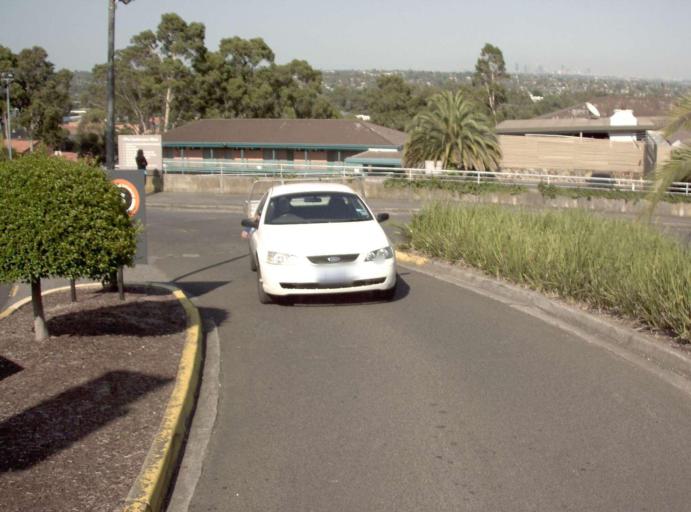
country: AU
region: Victoria
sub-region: Manningham
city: Doncaster
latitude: -37.7847
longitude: 145.1241
